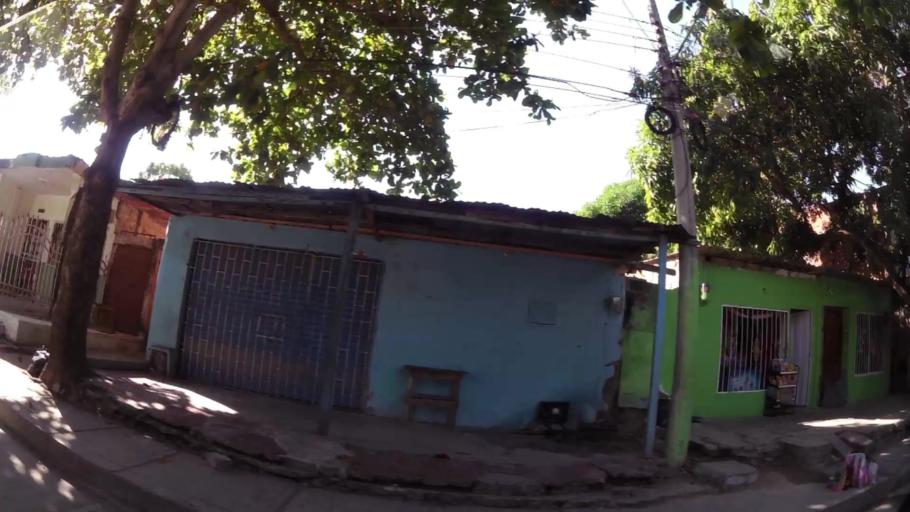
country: CO
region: Bolivar
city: Cartagena
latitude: 10.3704
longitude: -75.5029
